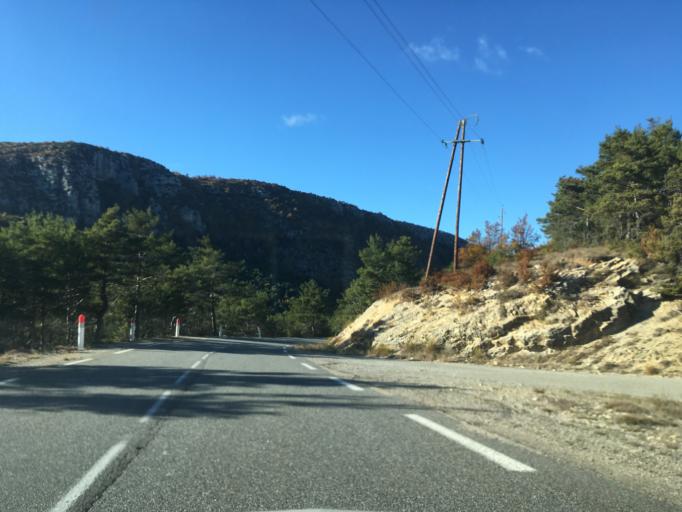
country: FR
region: Provence-Alpes-Cote d'Azur
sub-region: Departement du Var
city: Bargemon
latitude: 43.7272
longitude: 6.5034
